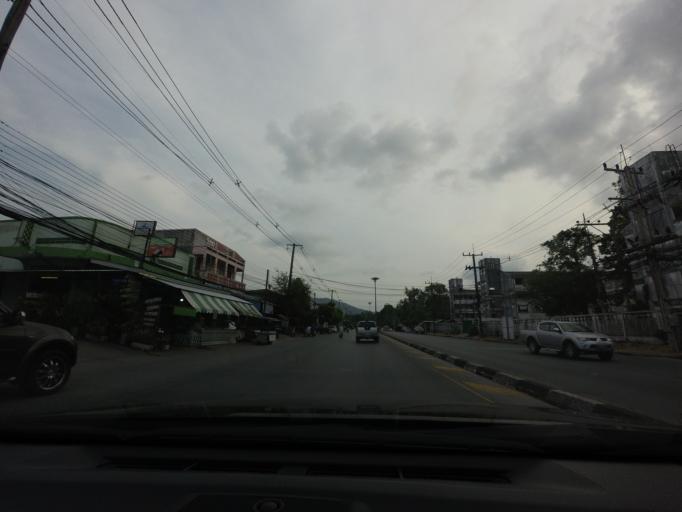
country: TH
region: Yala
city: Yala
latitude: 6.5263
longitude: 101.2827
